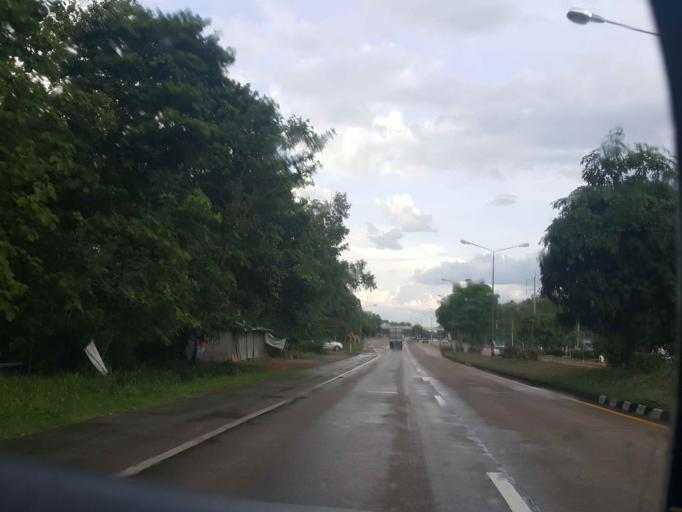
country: TH
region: Phrae
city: Den Chai
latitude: 17.9852
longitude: 100.0945
